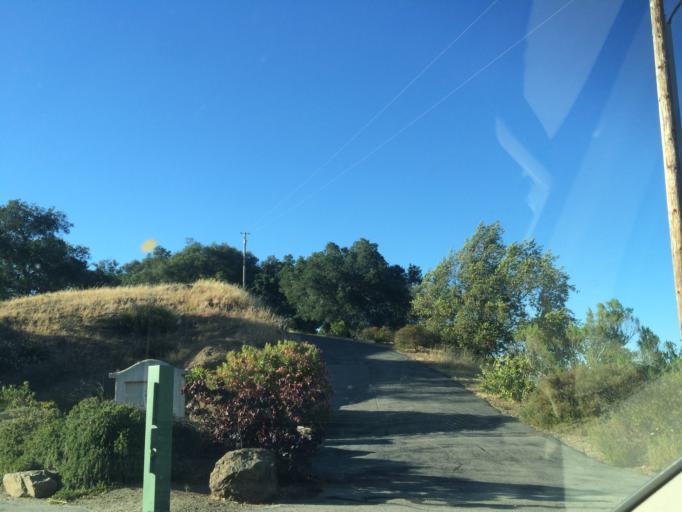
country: US
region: California
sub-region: San Luis Obispo County
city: Atascadero
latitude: 35.4527
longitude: -120.7174
